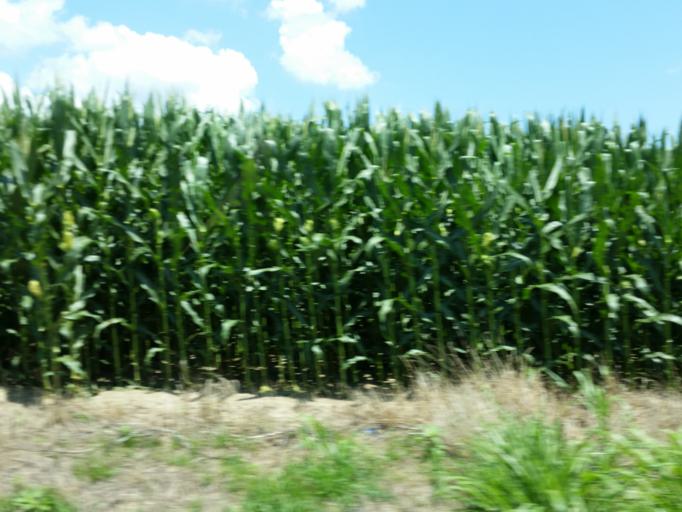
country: US
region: Kentucky
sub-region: Fulton County
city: Hickman
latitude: 36.5583
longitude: -89.2873
